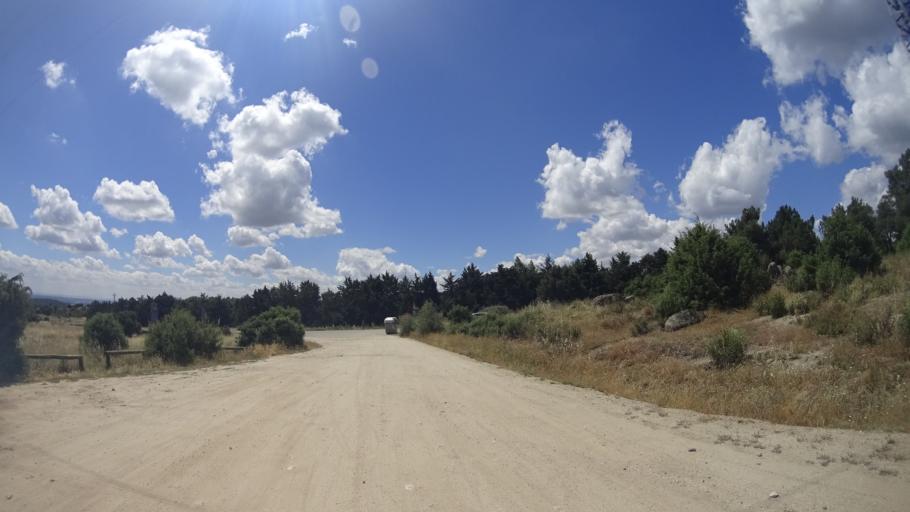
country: ES
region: Madrid
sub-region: Provincia de Madrid
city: Hoyo de Manzanares
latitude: 40.6016
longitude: -3.9153
